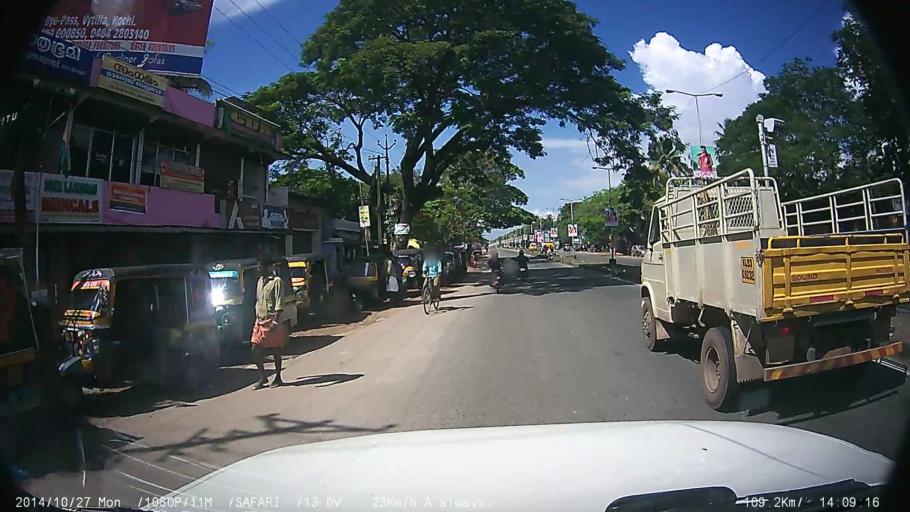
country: IN
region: Kerala
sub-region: Alappuzha
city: Kutiatodu
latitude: 9.7686
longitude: 76.3182
